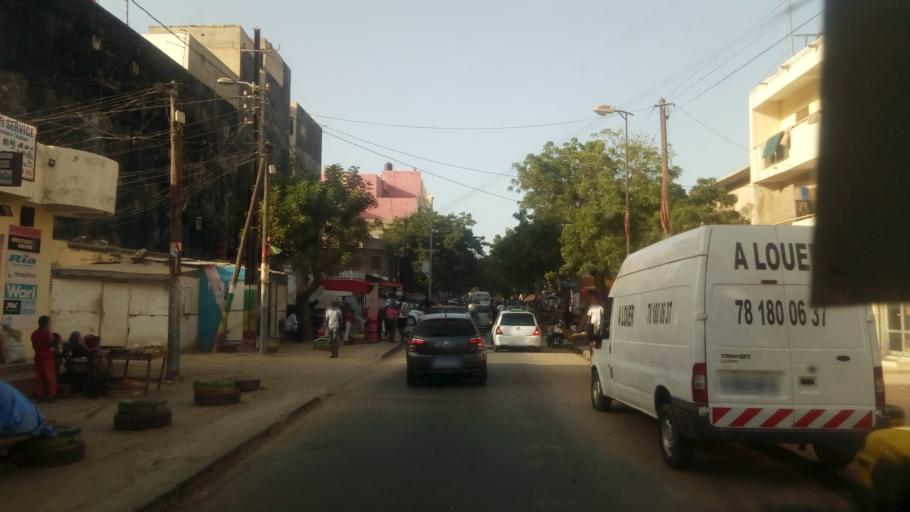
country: SN
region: Dakar
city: Grand Dakar
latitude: 14.7114
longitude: -17.4497
